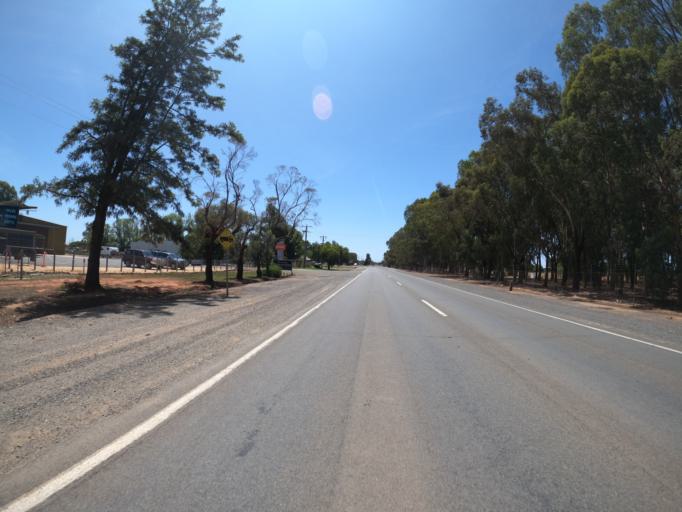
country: AU
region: Victoria
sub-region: Moira
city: Yarrawonga
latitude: -36.0340
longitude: 145.9955
